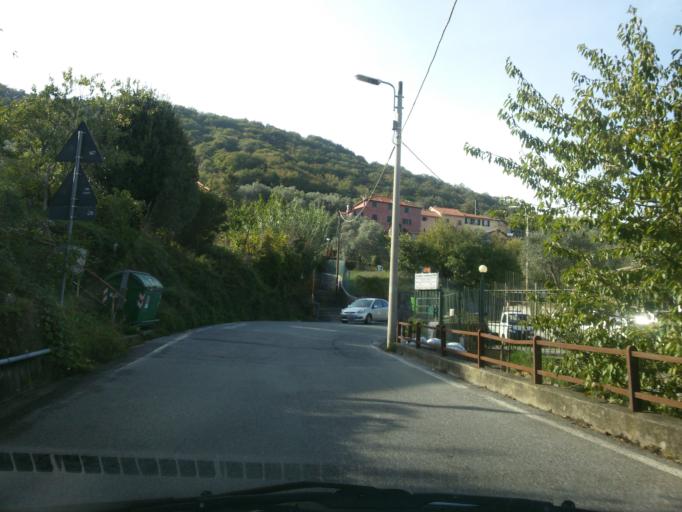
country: IT
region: Liguria
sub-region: Provincia di Genova
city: Piccarello
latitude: 44.4578
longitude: 8.9725
